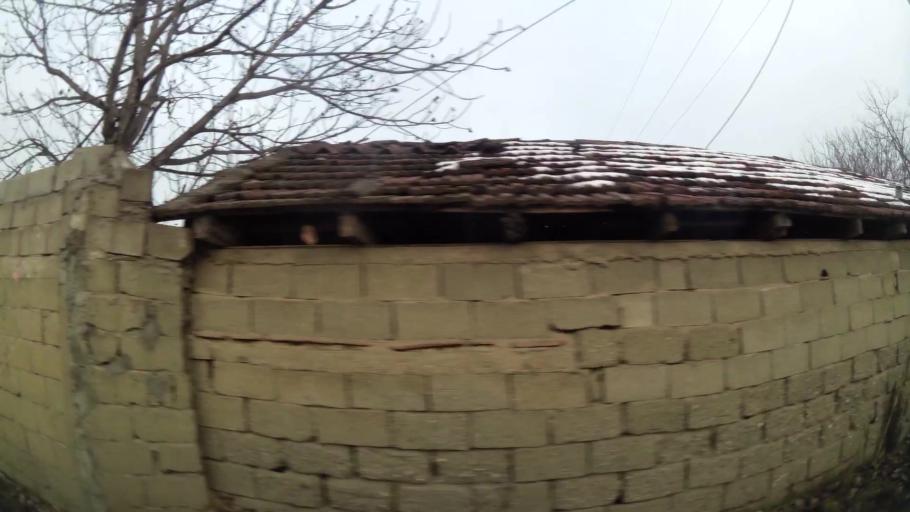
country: MK
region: Suto Orizari
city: Suto Orizare
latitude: 42.0287
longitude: 21.4195
